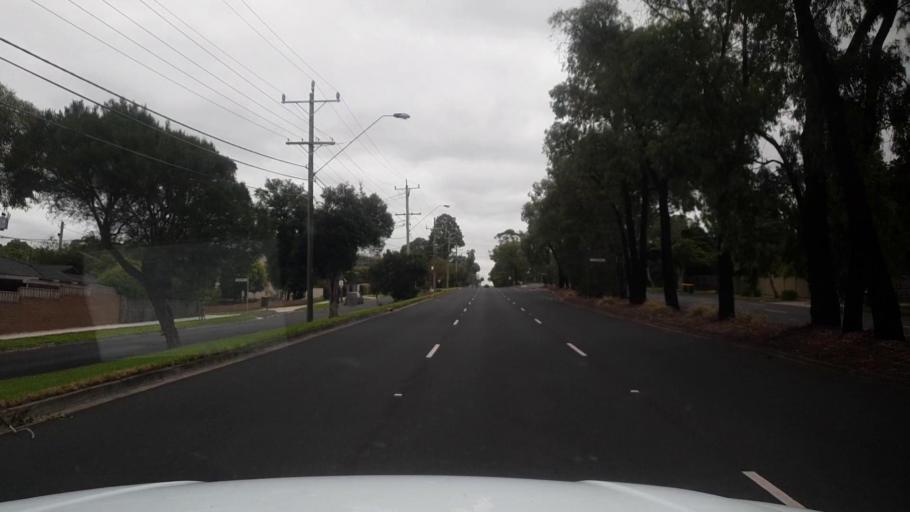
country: AU
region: Victoria
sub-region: Whitehorse
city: Vermont
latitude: -37.8343
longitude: 145.2045
